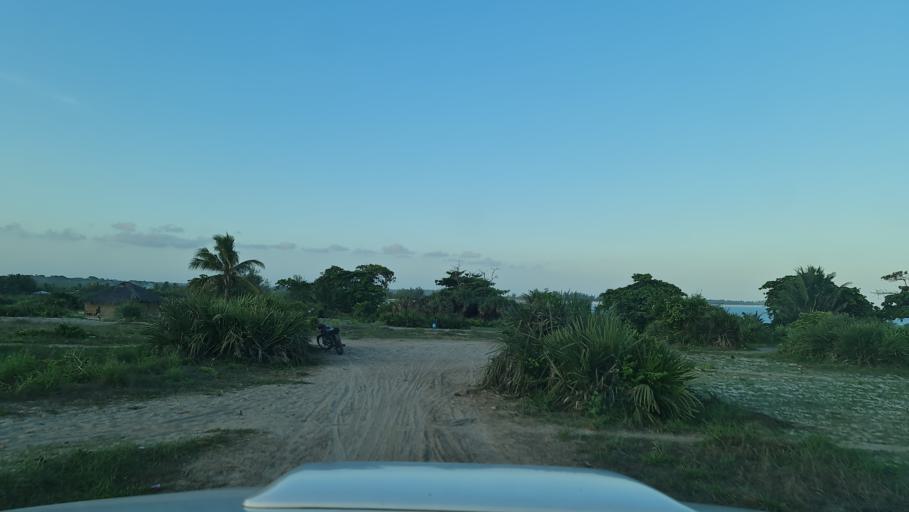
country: MZ
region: Nampula
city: Ilha de Mocambique
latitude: -15.6279
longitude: 40.4223
